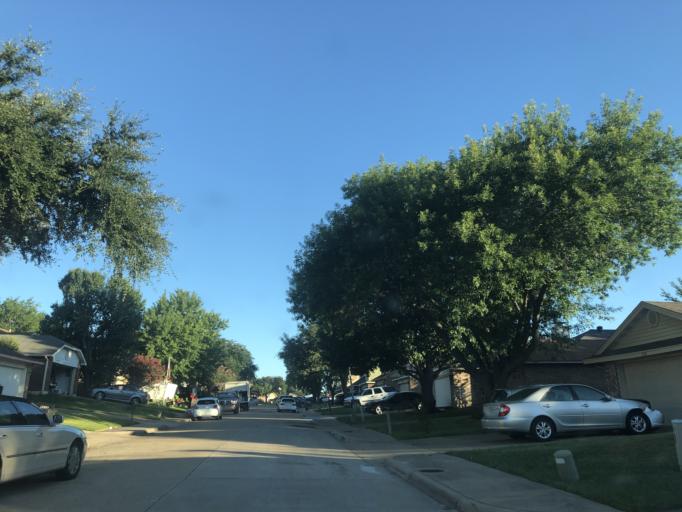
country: US
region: Texas
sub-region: Dallas County
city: Garland
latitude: 32.8363
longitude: -96.6348
